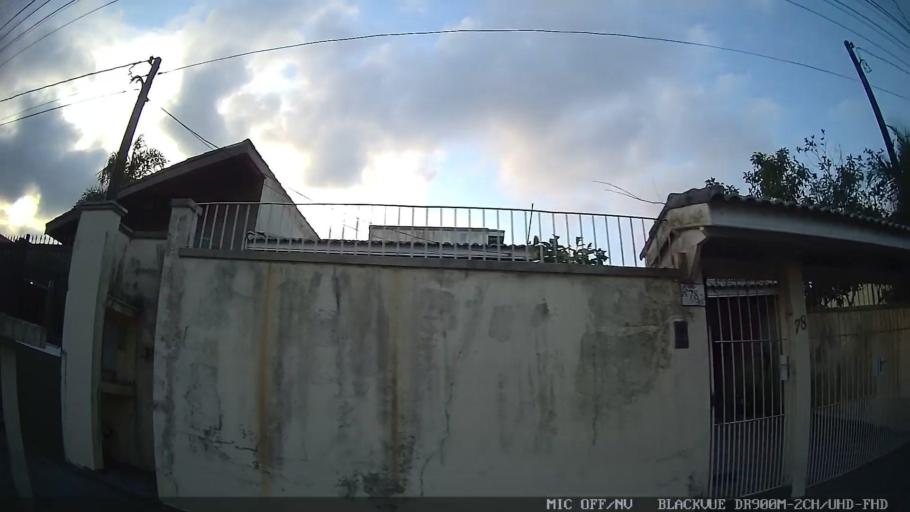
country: BR
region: Sao Paulo
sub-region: Peruibe
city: Peruibe
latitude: -24.3245
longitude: -47.0009
